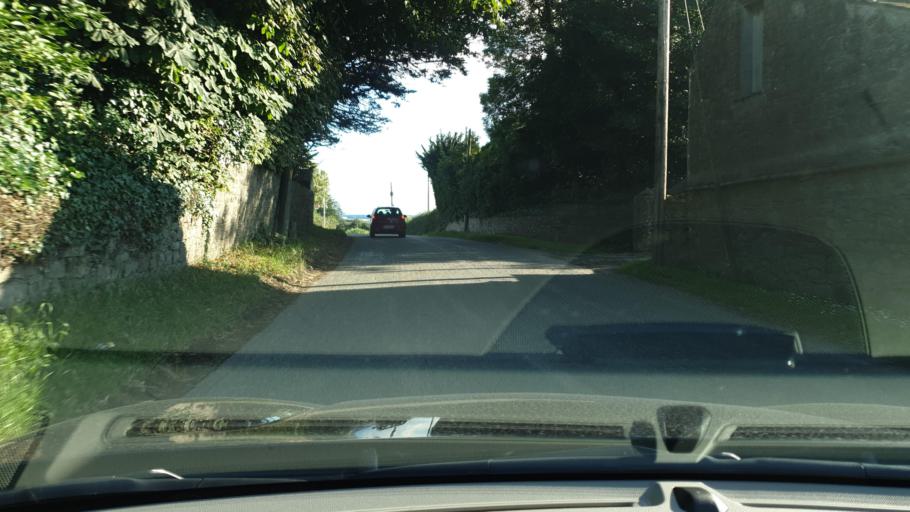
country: IE
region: Leinster
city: Lusk
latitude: 53.5396
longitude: -6.1927
